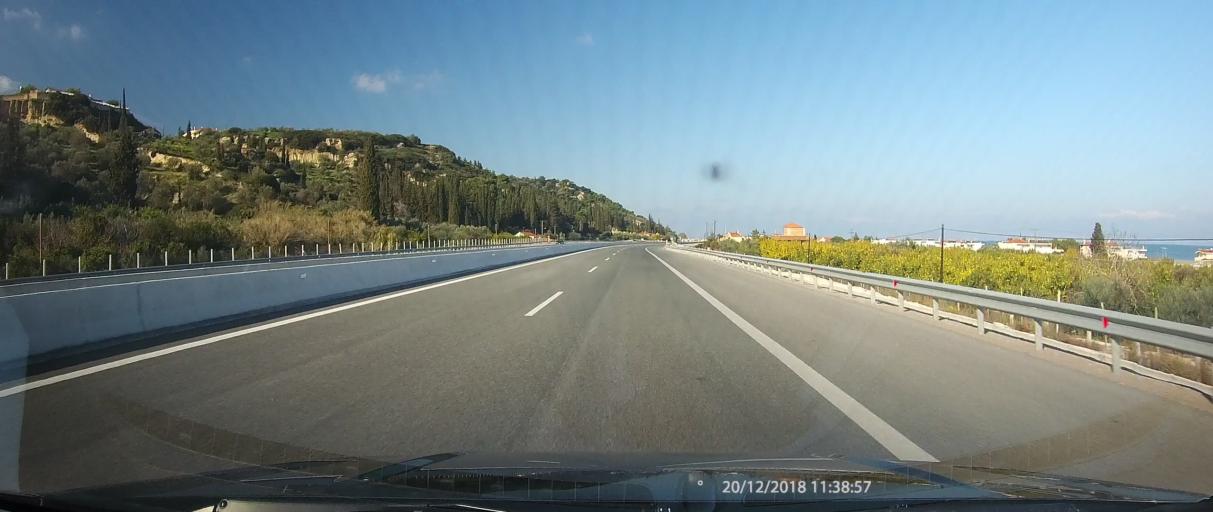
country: GR
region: Peloponnese
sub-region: Nomos Korinthias
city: Kato Dhiminio
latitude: 38.0351
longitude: 22.7136
